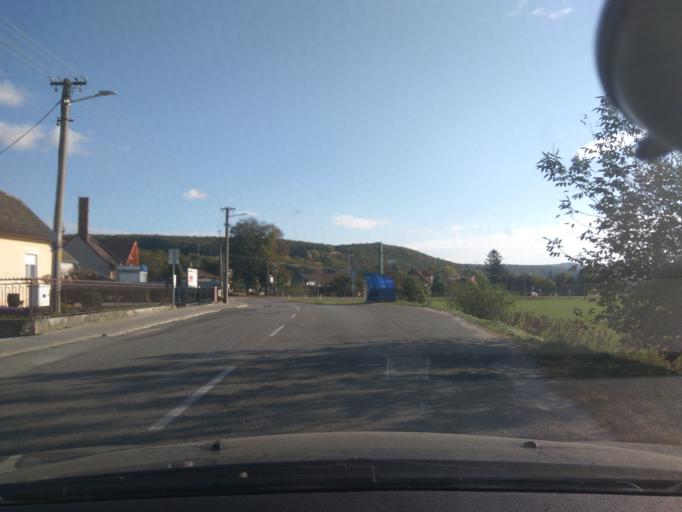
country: SK
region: Trnavsky
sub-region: Okres Trnava
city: Piestany
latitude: 48.5496
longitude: 17.8431
